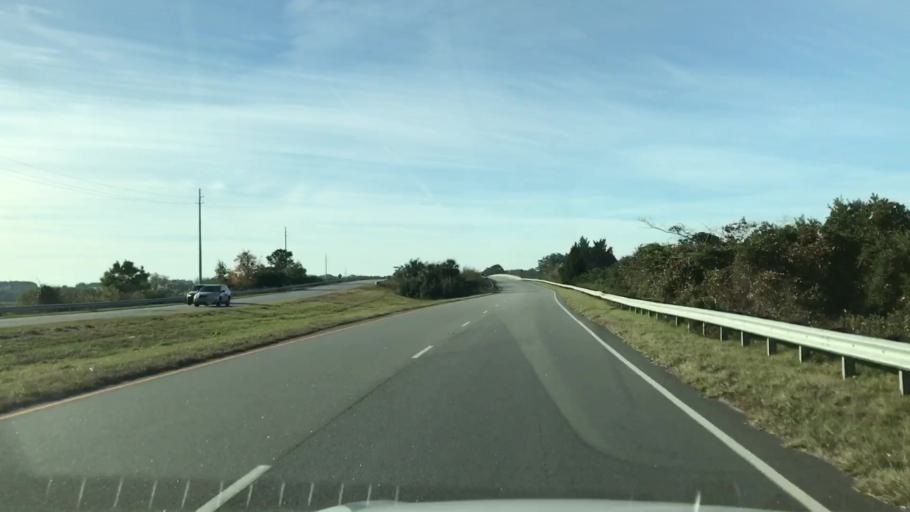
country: US
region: South Carolina
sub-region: Beaufort County
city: Laurel Bay
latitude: 32.5439
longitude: -80.7447
